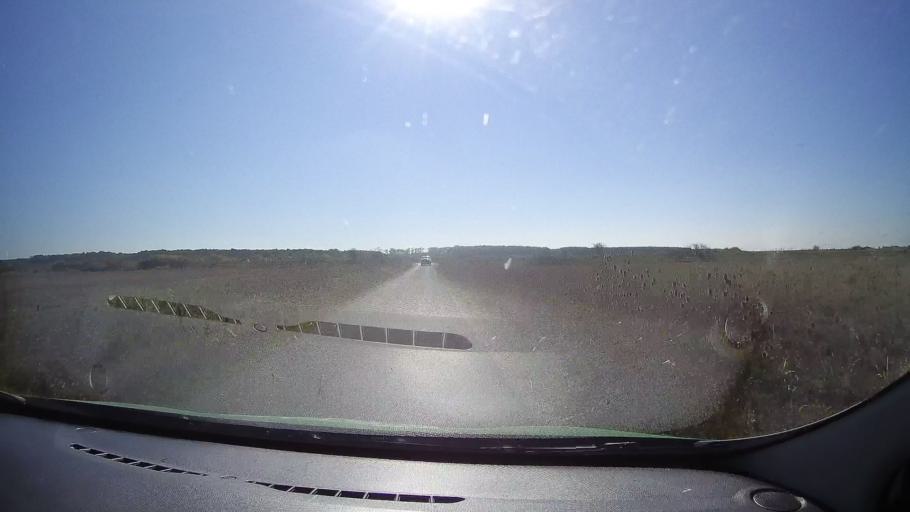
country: RO
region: Satu Mare
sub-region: Comuna Doba
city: Doba
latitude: 47.7247
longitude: 22.7243
